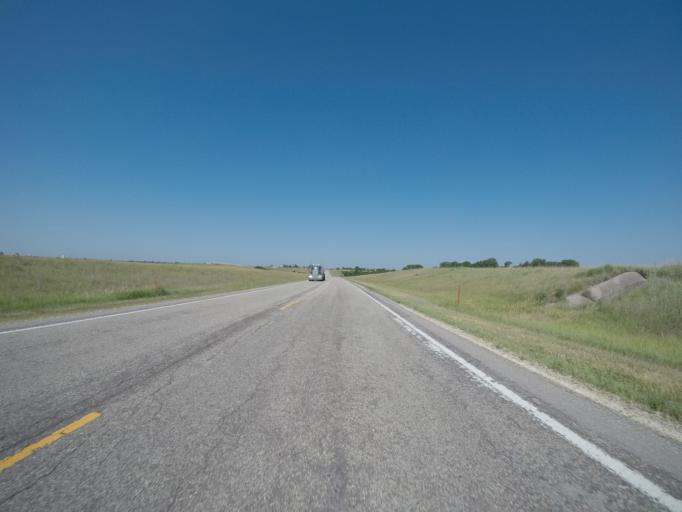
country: US
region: Kansas
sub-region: Clay County
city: Clay Center
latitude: 39.3648
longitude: -97.4272
